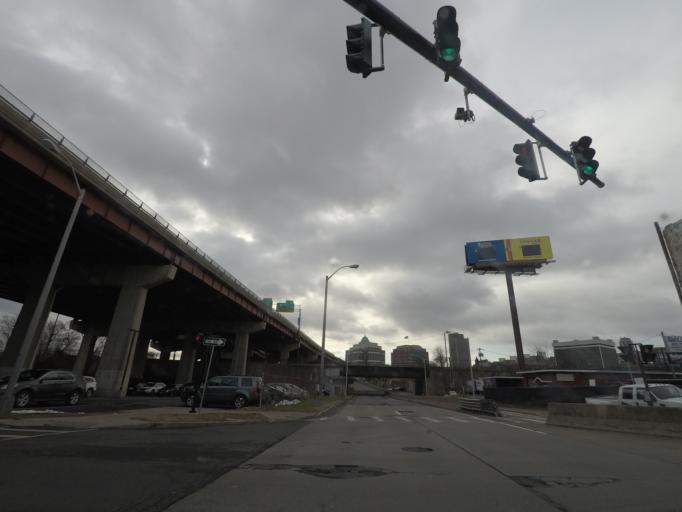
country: US
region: New York
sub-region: Albany County
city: Albany
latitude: 42.6562
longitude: -73.7438
